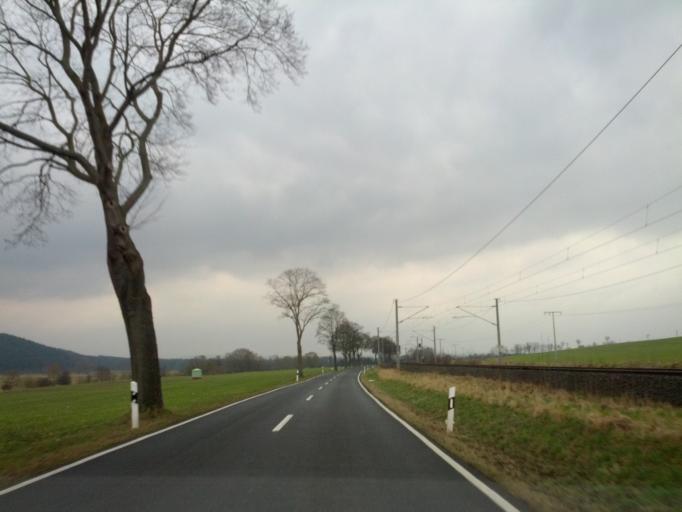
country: DE
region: Thuringia
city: Gerstungen
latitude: 50.9870
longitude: 10.0956
